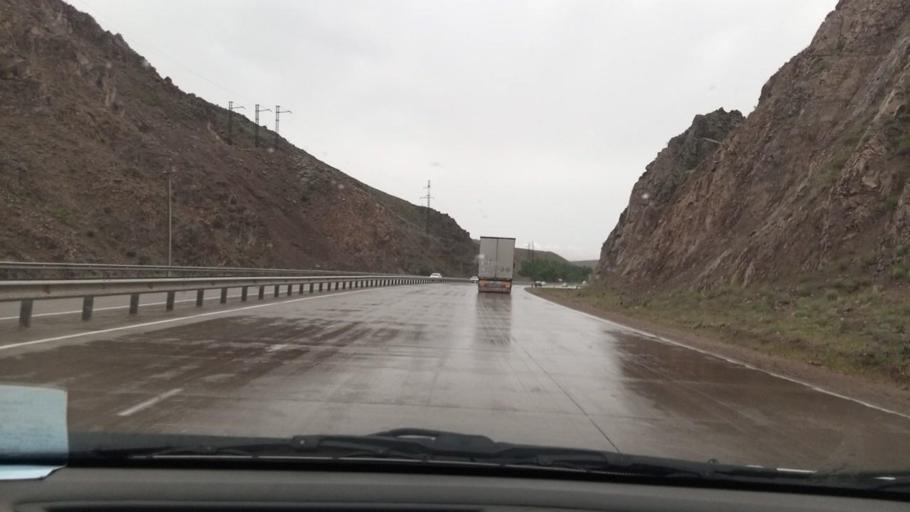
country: TJ
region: Viloyati Sughd
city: Shaydon
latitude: 40.9557
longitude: 70.6717
